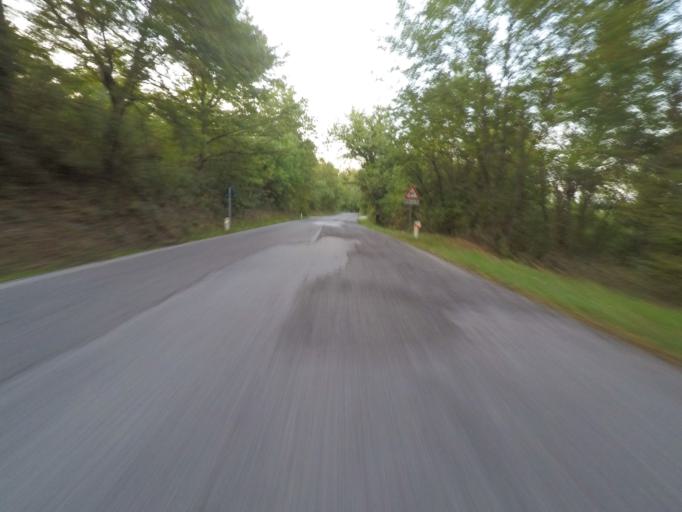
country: IT
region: Tuscany
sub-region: Provincia di Siena
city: Torrita di Siena
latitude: 43.1424
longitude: 11.7355
